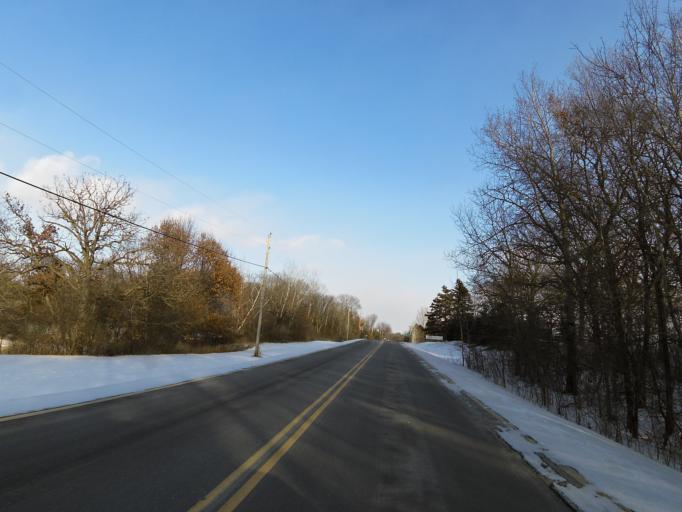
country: US
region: Minnesota
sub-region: Washington County
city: Lake Elmo
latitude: 44.9780
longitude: -92.8759
